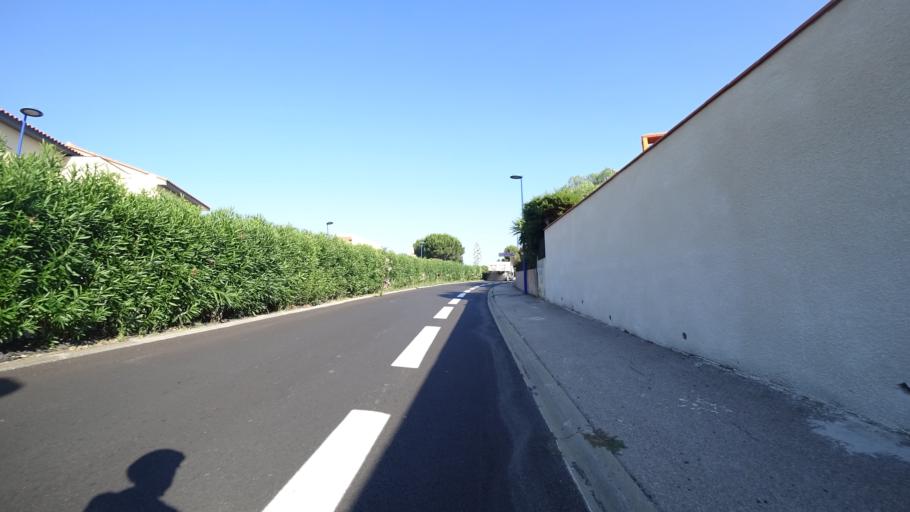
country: FR
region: Languedoc-Roussillon
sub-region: Departement des Pyrenees-Orientales
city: Cabestany
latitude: 42.6849
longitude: 2.9410
